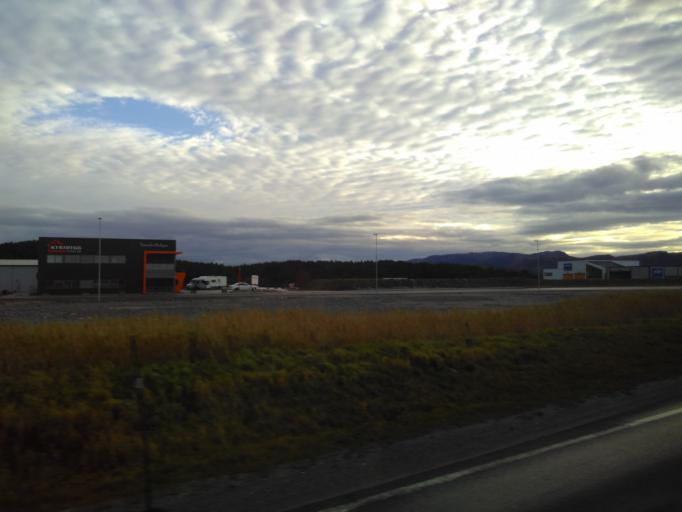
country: NO
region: Sor-Trondelag
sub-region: Hitra
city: Fillan
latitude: 63.5204
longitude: 9.1087
